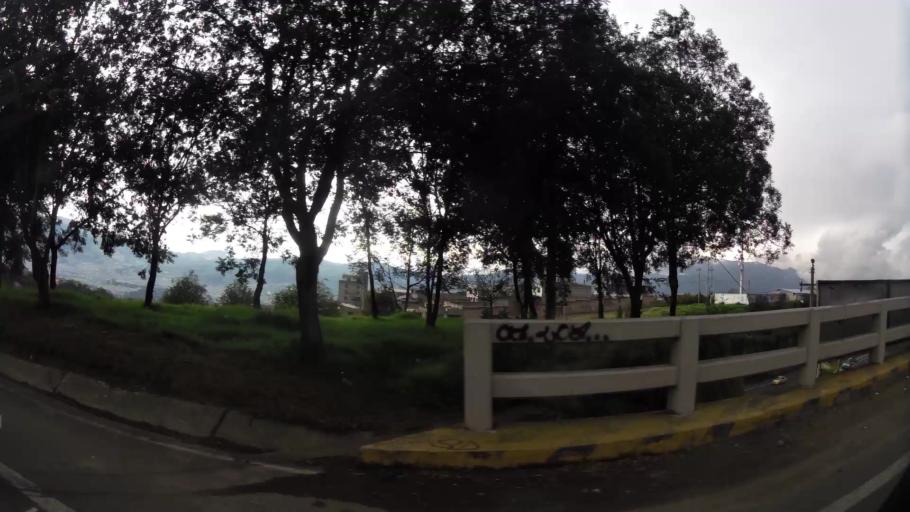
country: EC
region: Pichincha
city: Quito
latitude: -0.2887
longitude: -78.5199
